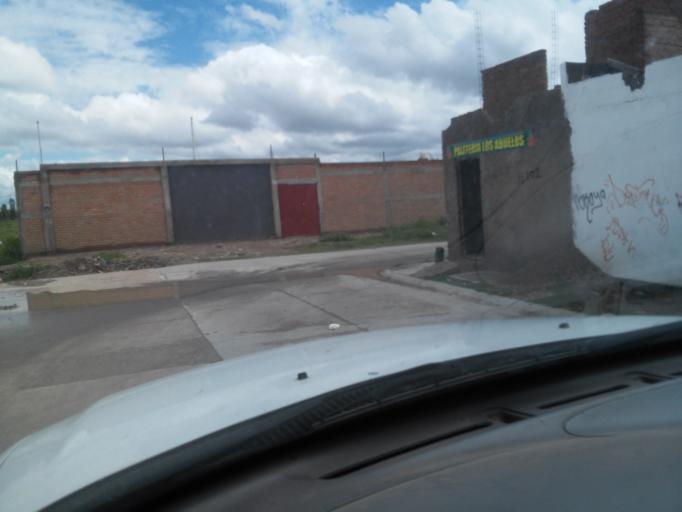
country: MX
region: Durango
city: Victoria de Durango
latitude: 24.0211
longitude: -104.6104
